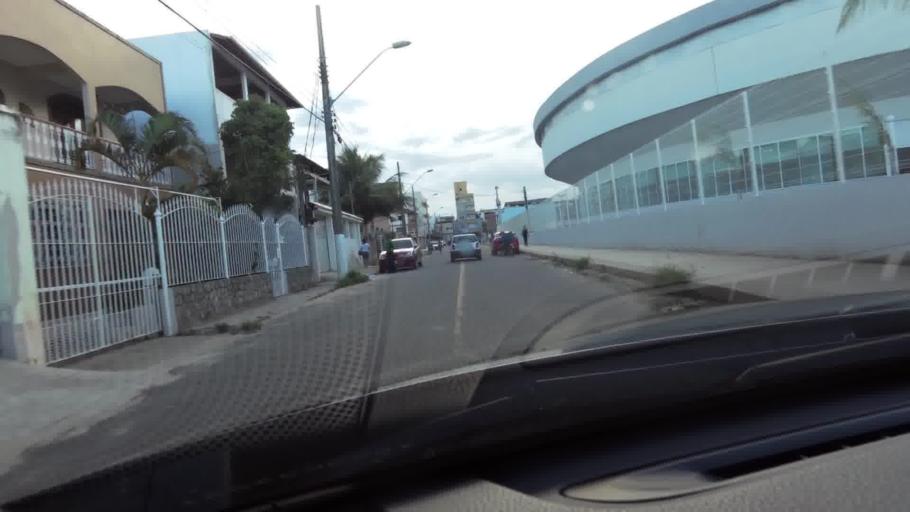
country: BR
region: Espirito Santo
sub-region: Guarapari
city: Guarapari
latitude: -20.6594
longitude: -40.4998
